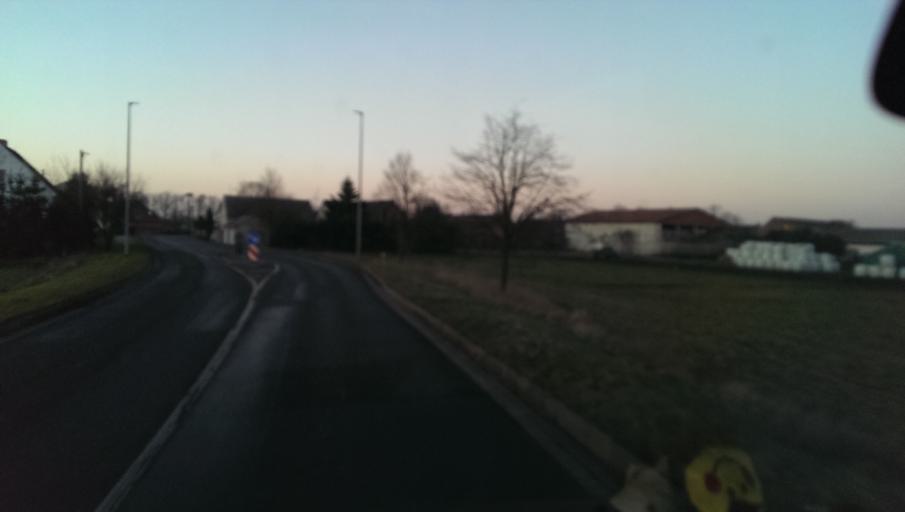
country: DE
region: Saxony-Anhalt
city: Holzdorf
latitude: 51.8159
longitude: 13.1639
